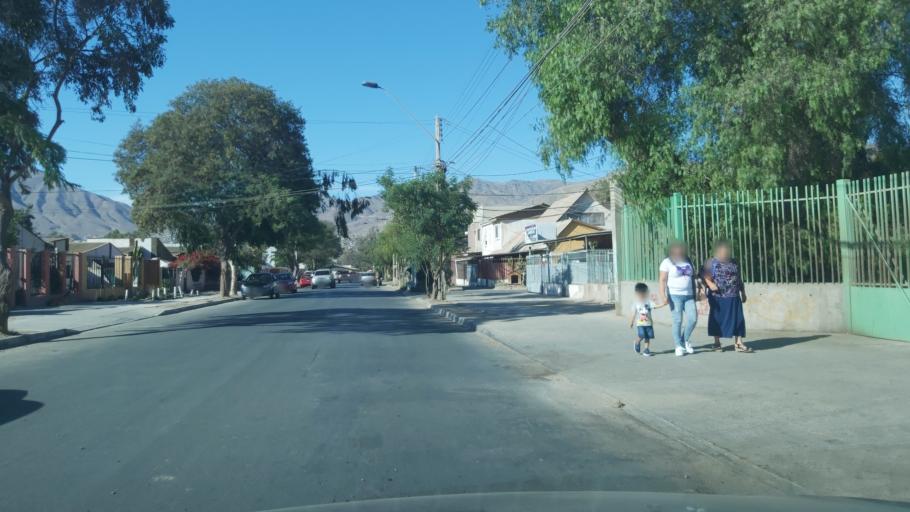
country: CL
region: Atacama
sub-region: Provincia de Copiapo
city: Copiapo
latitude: -27.3756
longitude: -70.3209
